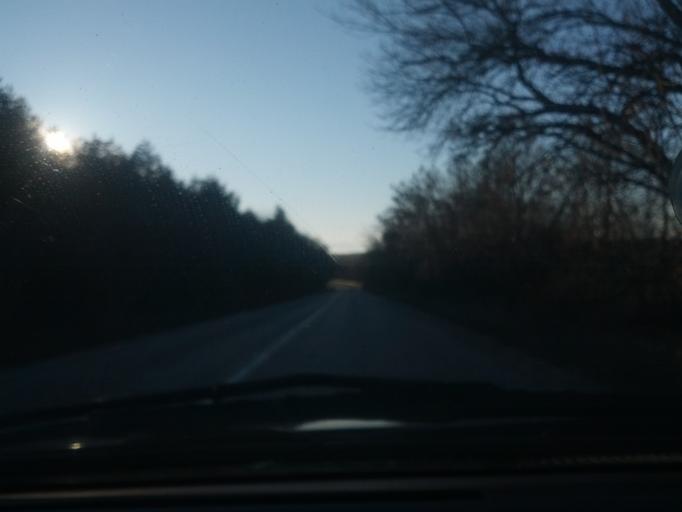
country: BG
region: Vratsa
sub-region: Obshtina Borovan
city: Borovan
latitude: 43.3718
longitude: 23.7062
